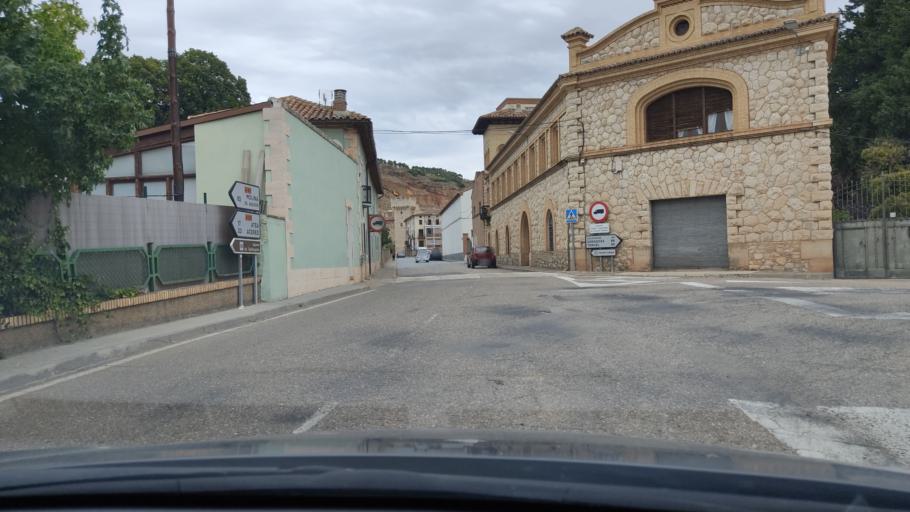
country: ES
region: Aragon
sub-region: Provincia de Zaragoza
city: Daroca
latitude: 41.1107
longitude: -1.4178
